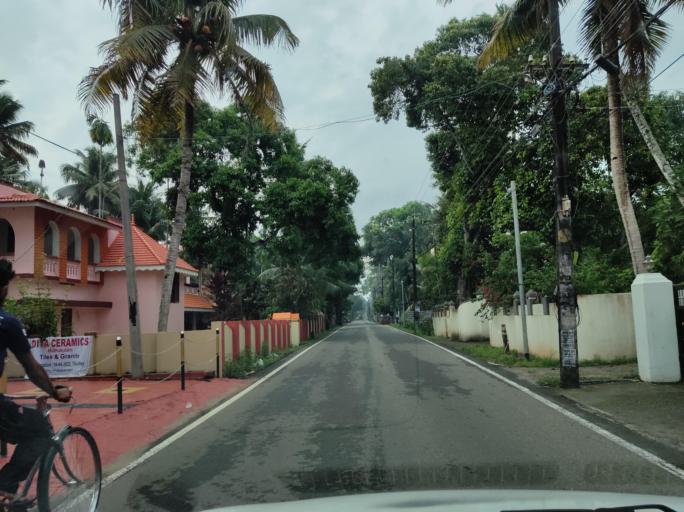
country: IN
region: Kerala
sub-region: Alappuzha
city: Kayankulam
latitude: 9.2218
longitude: 76.4602
